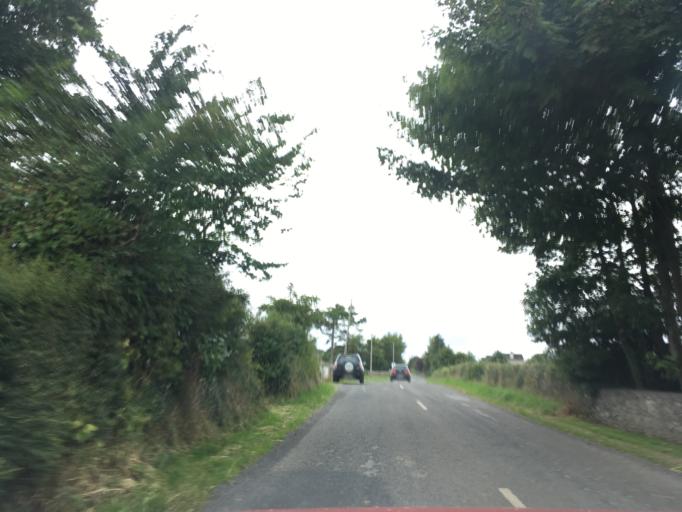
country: IE
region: Munster
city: Cahir
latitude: 52.4582
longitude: -7.9763
